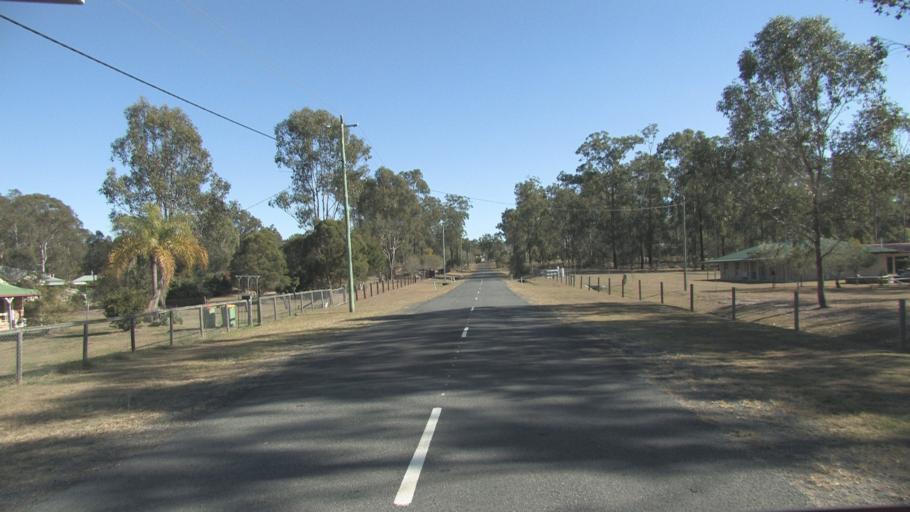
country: AU
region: Queensland
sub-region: Logan
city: North Maclean
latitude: -27.8112
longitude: 152.9674
